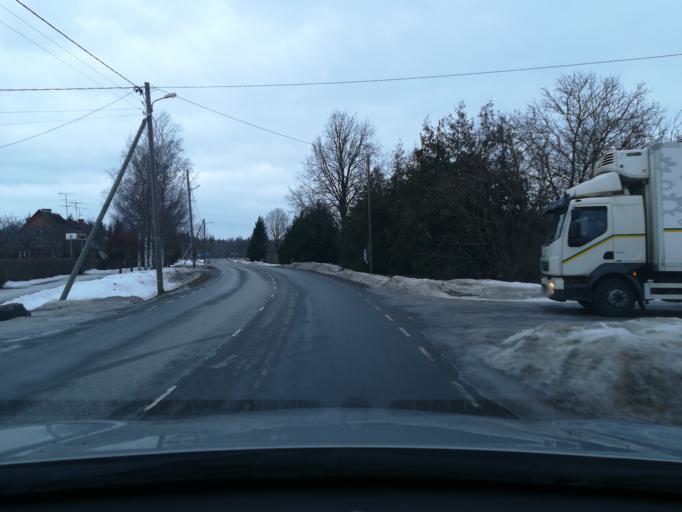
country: EE
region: Harju
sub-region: Nissi vald
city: Turba
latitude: 59.0811
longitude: 24.2361
